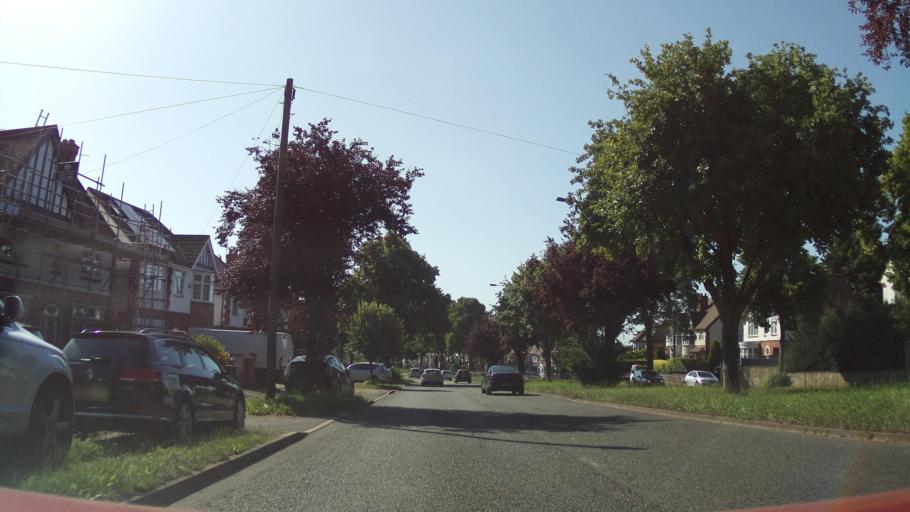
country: GB
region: England
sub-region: Derby
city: Derby
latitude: 52.9062
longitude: -1.4991
